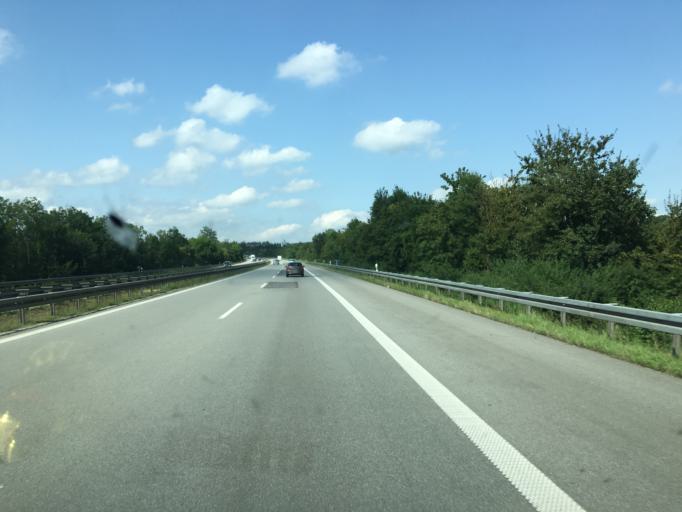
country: DE
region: Bavaria
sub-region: Lower Bavaria
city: Passau
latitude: 48.5091
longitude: 13.3898
